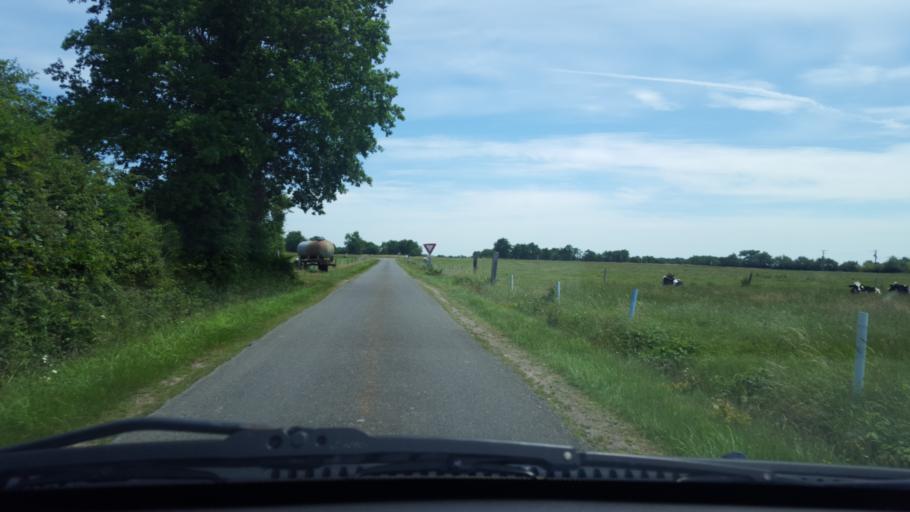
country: FR
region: Pays de la Loire
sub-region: Departement de la Loire-Atlantique
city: Geneston
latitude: 47.0482
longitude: -1.5674
